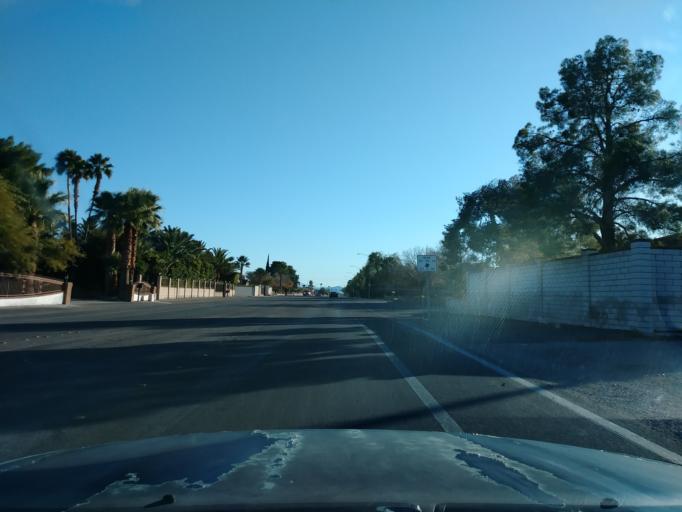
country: US
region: Nevada
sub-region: Clark County
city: Spring Valley
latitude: 36.1486
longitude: -115.2704
